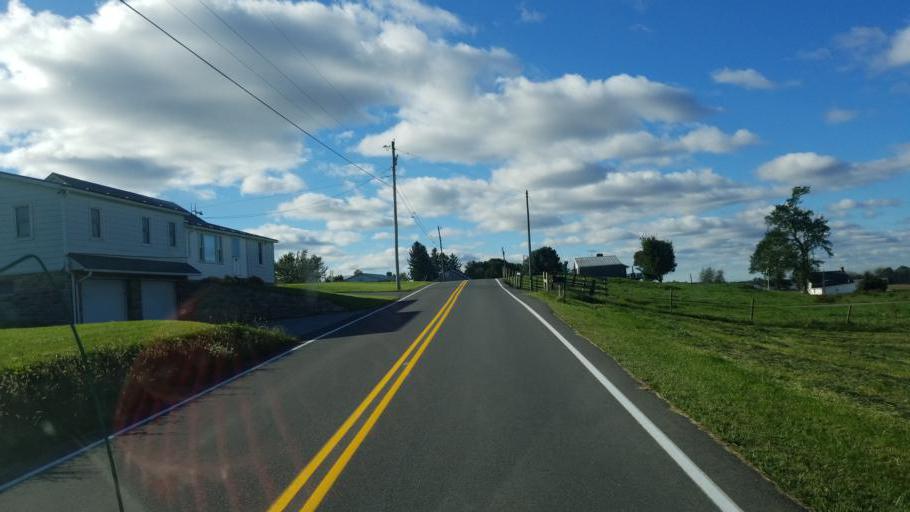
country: US
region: Pennsylvania
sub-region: Franklin County
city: Guilford Siding
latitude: 39.8229
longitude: -77.6395
